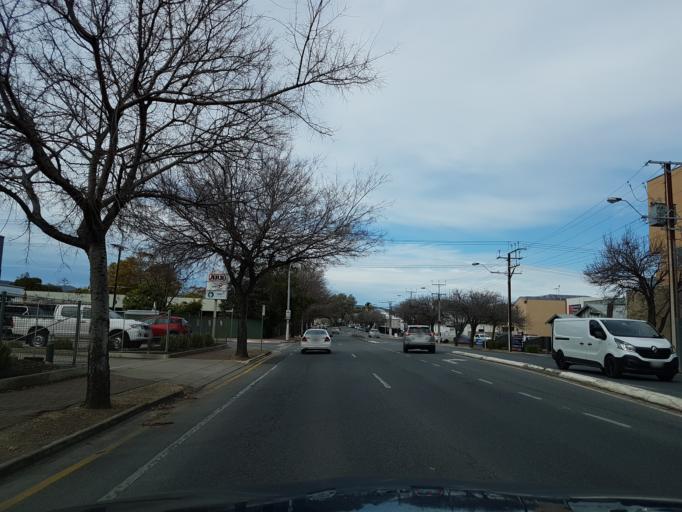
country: AU
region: South Australia
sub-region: Norwood Payneham St Peters
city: Trinity Gardens
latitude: -34.9120
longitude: 138.6296
